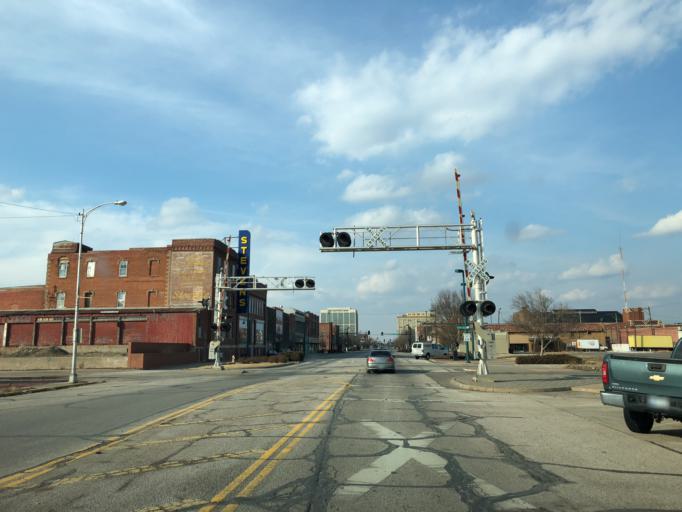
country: US
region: Kansas
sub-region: Reno County
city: Hutchinson
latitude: 38.0478
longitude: -97.9318
